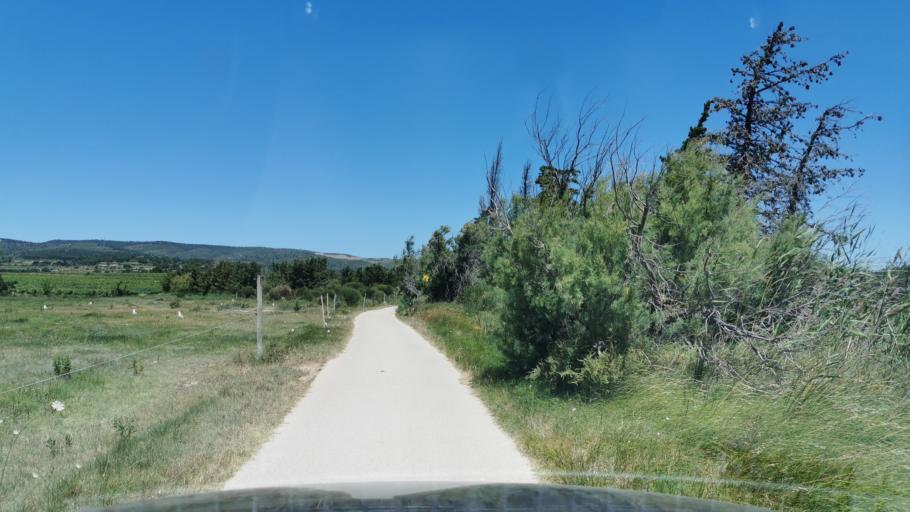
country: FR
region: Languedoc-Roussillon
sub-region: Departement de l'Aude
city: Peyriac-de-Mer
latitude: 43.1017
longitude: 2.9596
